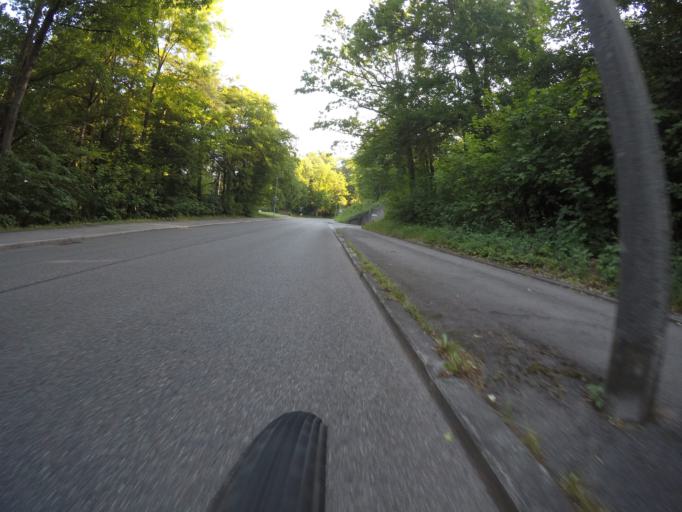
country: DE
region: Baden-Wuerttemberg
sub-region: Regierungsbezirk Stuttgart
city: Sindelfingen
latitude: 48.7143
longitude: 9.0209
